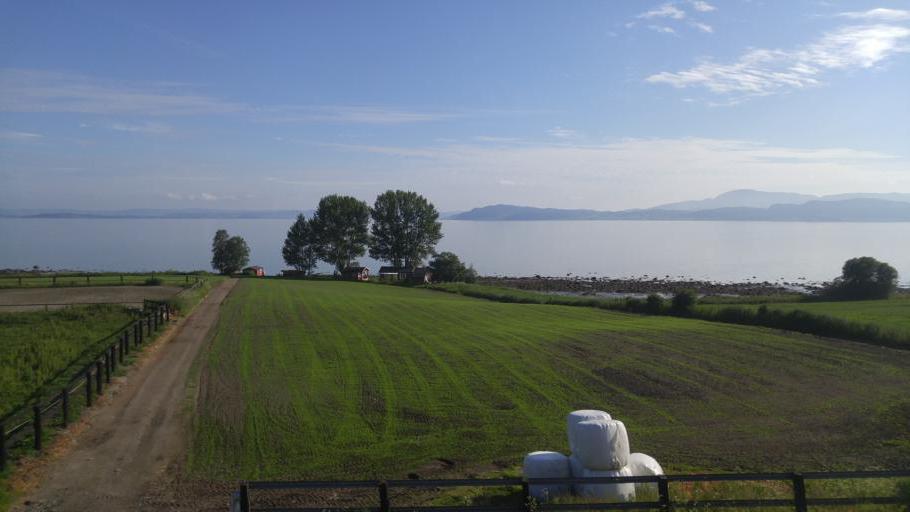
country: NO
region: Sor-Trondelag
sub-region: Malvik
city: Malvik
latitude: 63.4360
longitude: 10.6845
